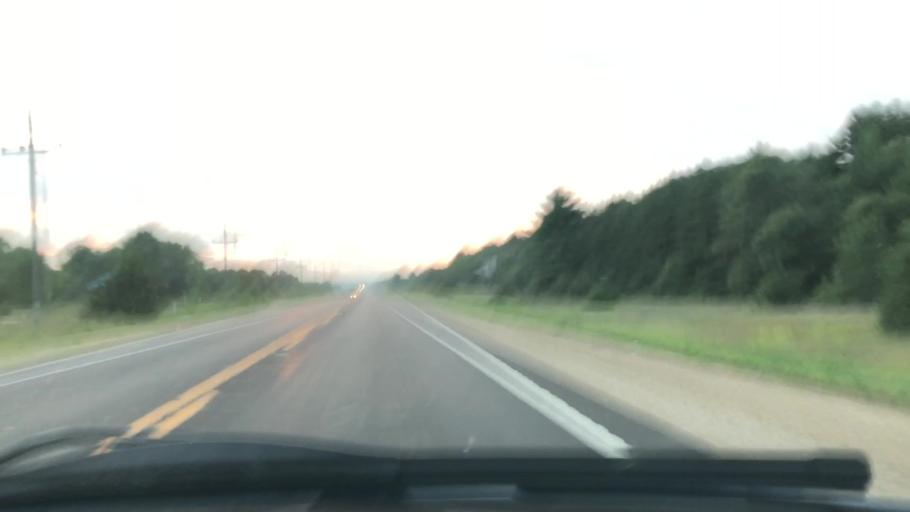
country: US
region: Wisconsin
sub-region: Sauk County
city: Spring Green
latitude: 43.1941
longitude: -90.2277
